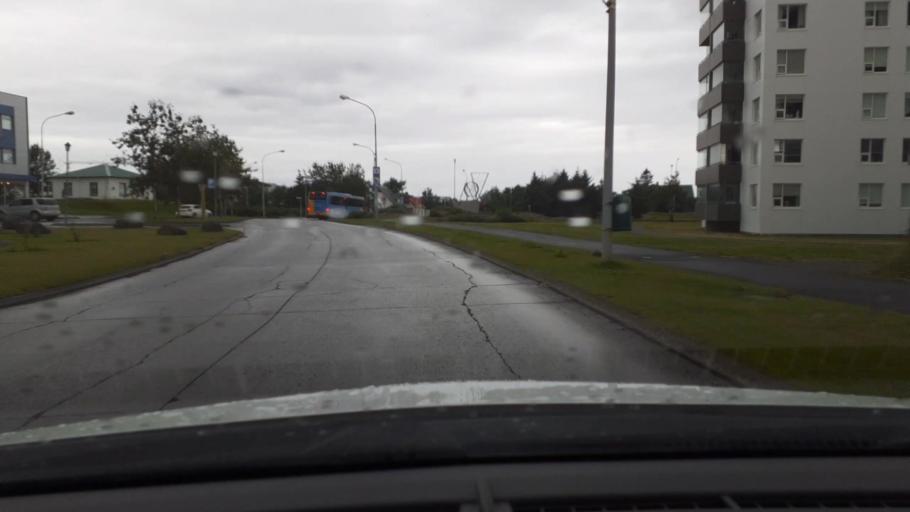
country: IS
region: West
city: Akranes
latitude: 64.3214
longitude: -22.0722
